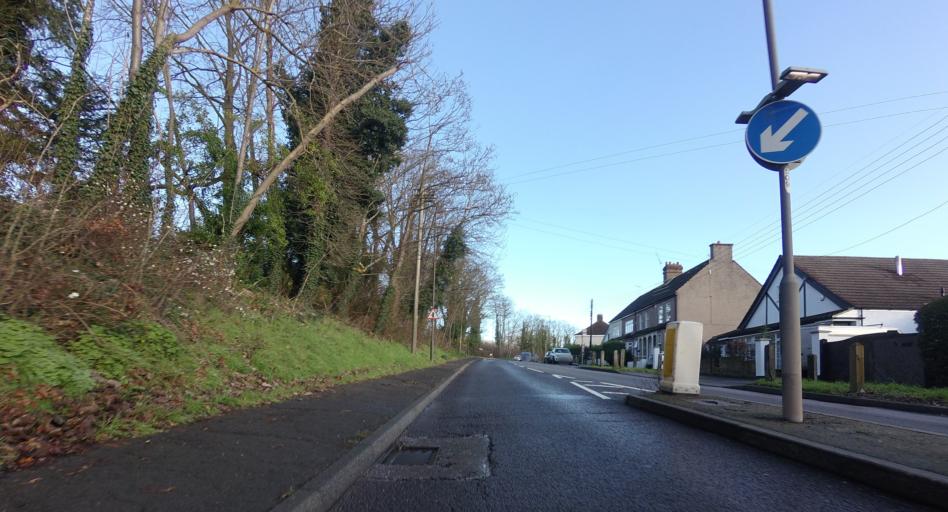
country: GB
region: England
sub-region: Kent
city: Swanley
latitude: 51.4143
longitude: 0.1849
